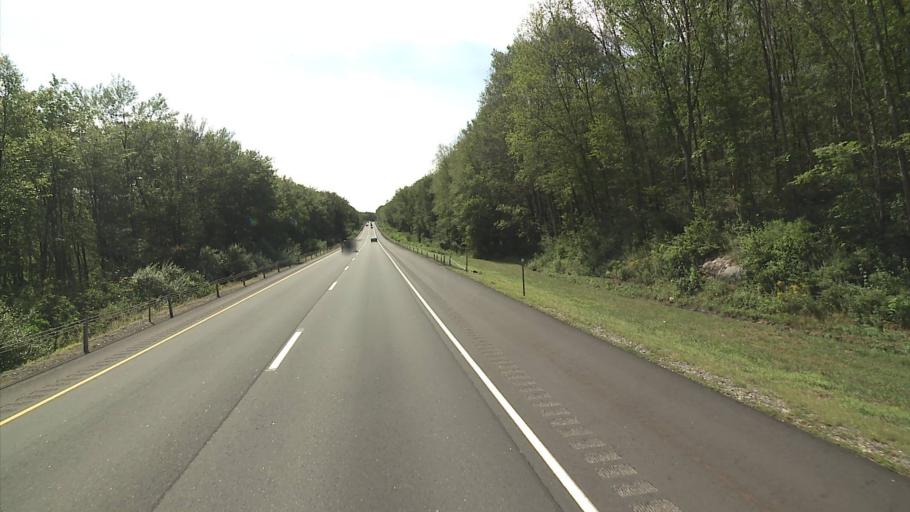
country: US
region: Connecticut
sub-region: Hartford County
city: Terramuggus
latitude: 41.6244
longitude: -72.4421
